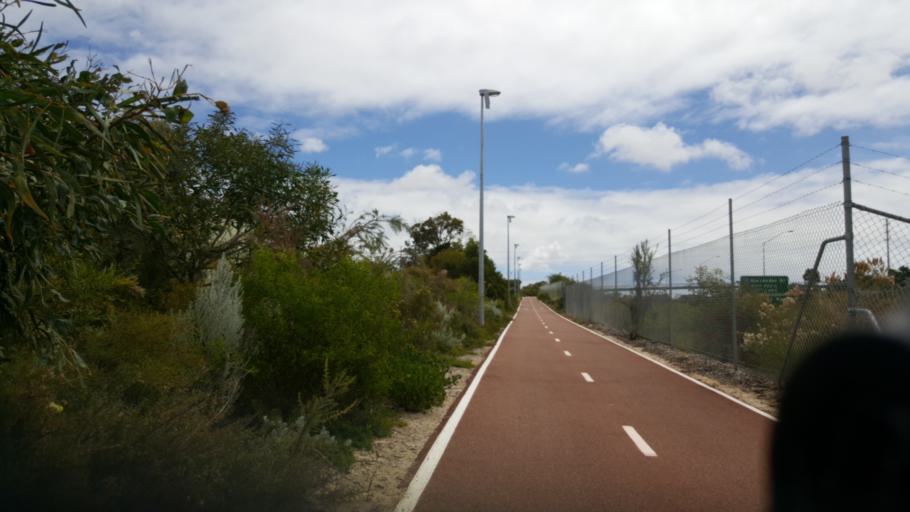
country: AU
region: Western Australia
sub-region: Bayswater
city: Embleton
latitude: -31.8684
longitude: 115.8913
